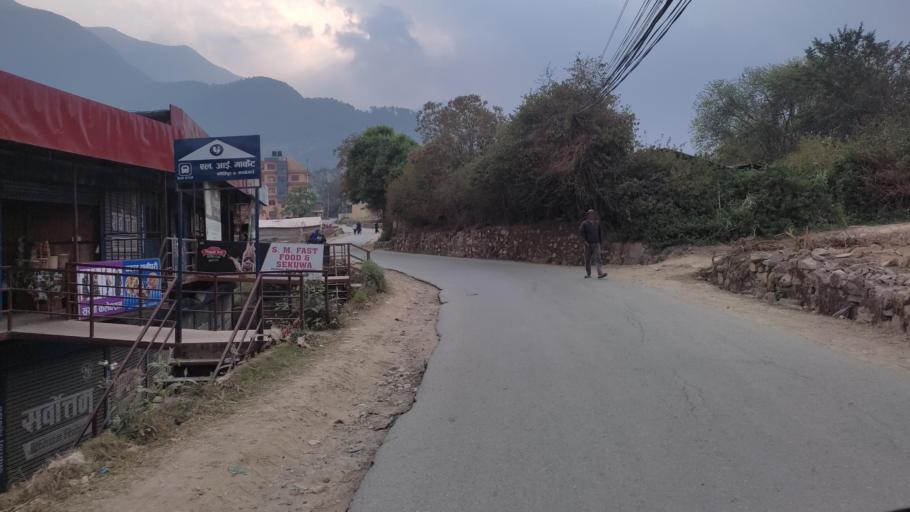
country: NP
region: Central Region
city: Kirtipur
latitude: 27.6670
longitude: 85.2608
